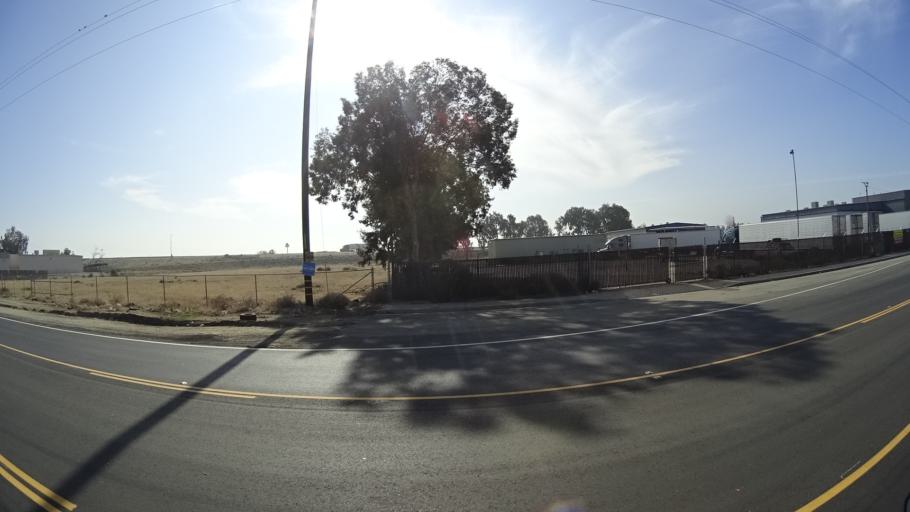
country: US
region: California
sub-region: Kern County
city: Bakersfield
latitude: 35.3542
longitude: -118.9526
